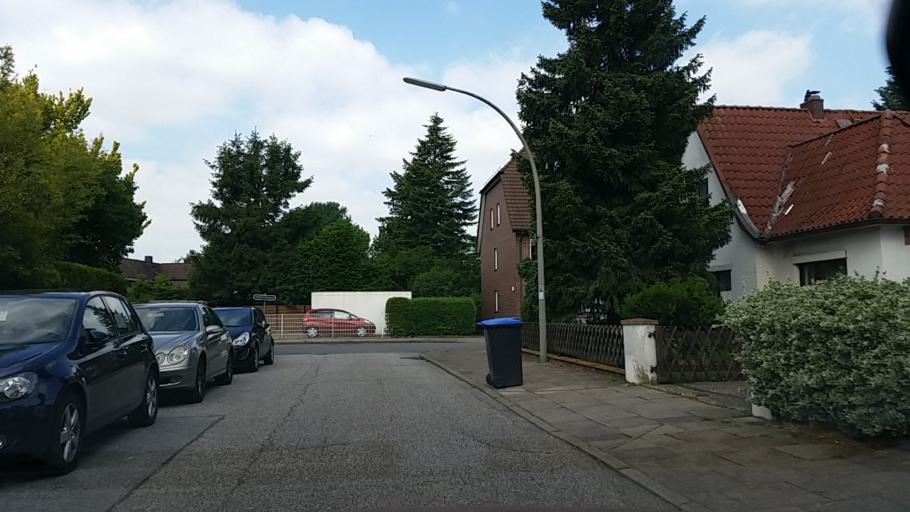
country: DE
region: Hamburg
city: Wandsbek
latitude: 53.5393
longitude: 10.1193
